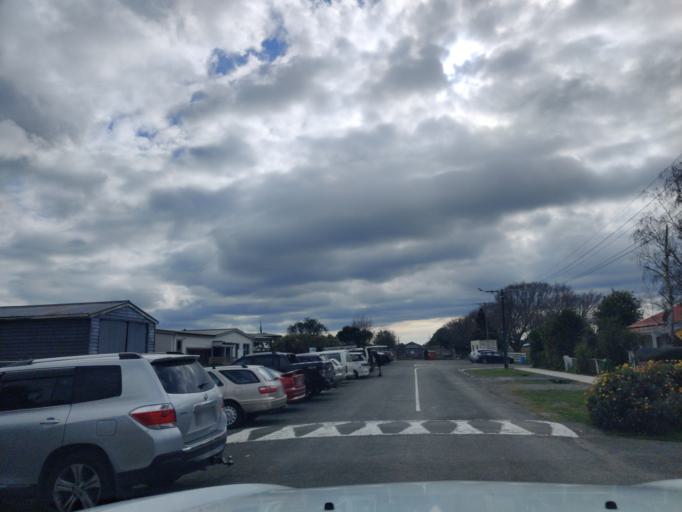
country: NZ
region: Manawatu-Wanganui
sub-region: Palmerston North City
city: Palmerston North
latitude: -40.2915
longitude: 175.7561
